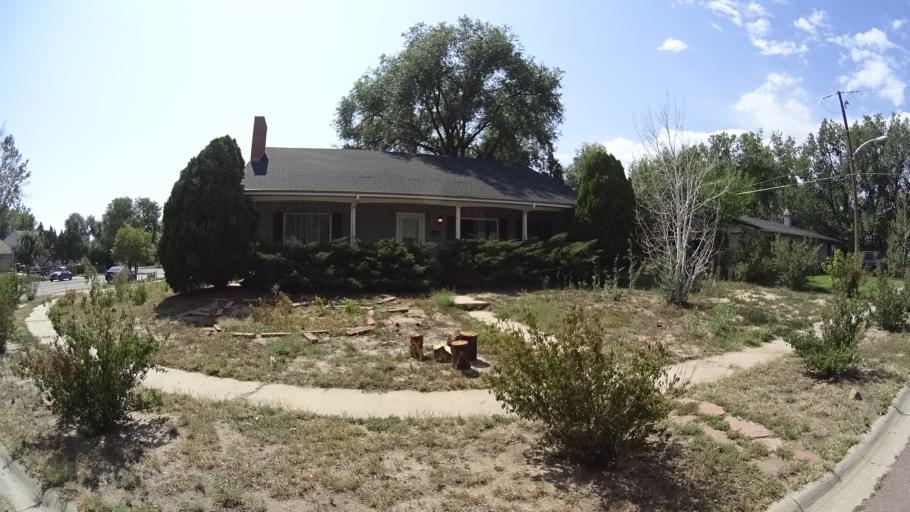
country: US
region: Colorado
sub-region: El Paso County
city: Colorado Springs
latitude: 38.8319
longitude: -104.7716
